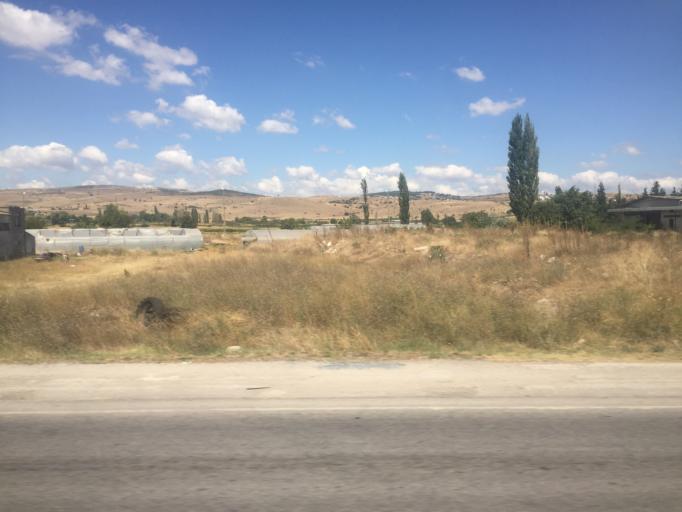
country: TR
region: Balikesir
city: Balikesir
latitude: 39.6828
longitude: 27.9404
